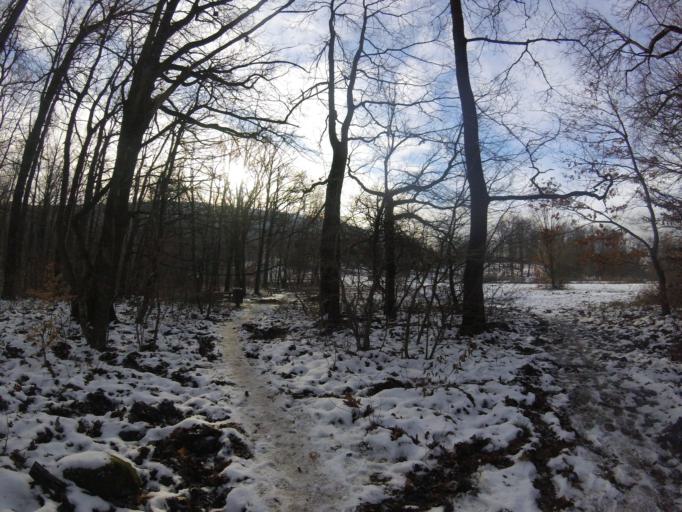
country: HU
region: Pest
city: Dunabogdany
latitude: 47.7388
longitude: 19.0136
